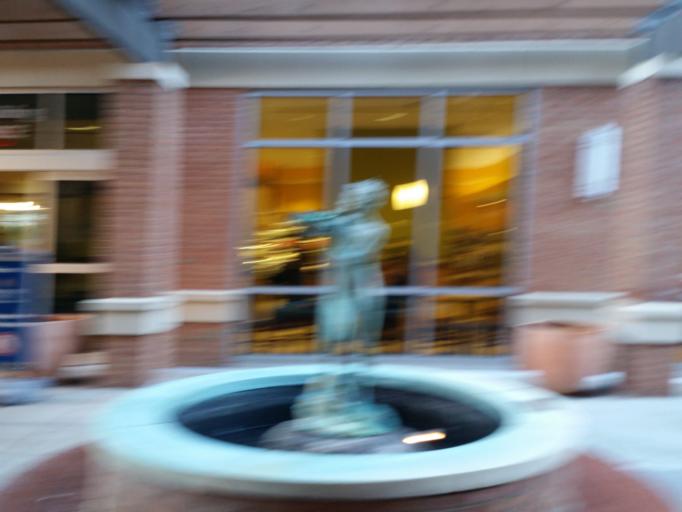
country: US
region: Maryland
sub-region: Montgomery County
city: Brookmont
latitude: 38.9369
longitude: -77.1072
